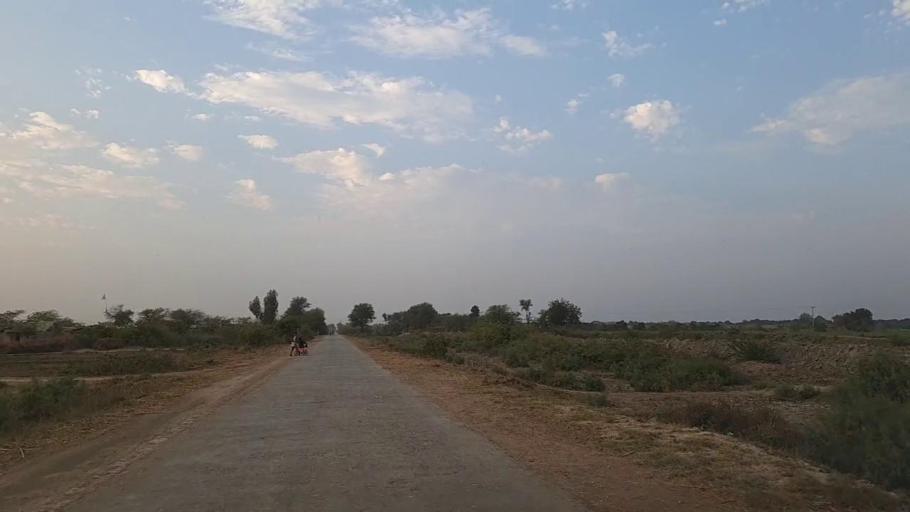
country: PK
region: Sindh
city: Mirwah Gorchani
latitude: 25.3356
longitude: 69.2104
